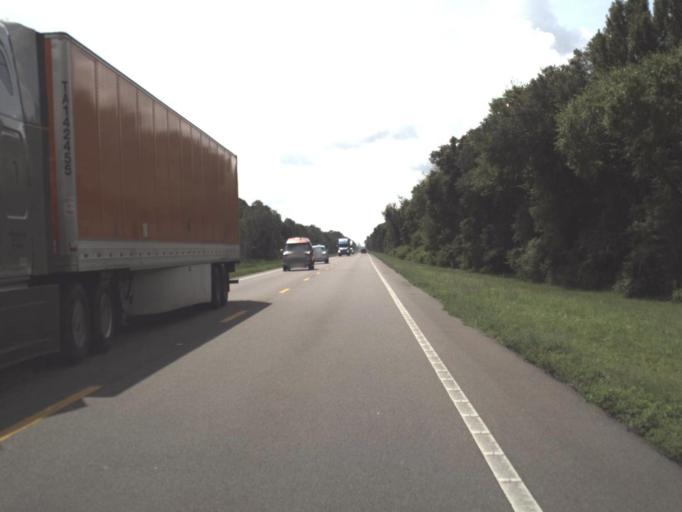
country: US
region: Florida
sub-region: Pasco County
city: Zephyrhills North
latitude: 28.2798
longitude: -82.1125
